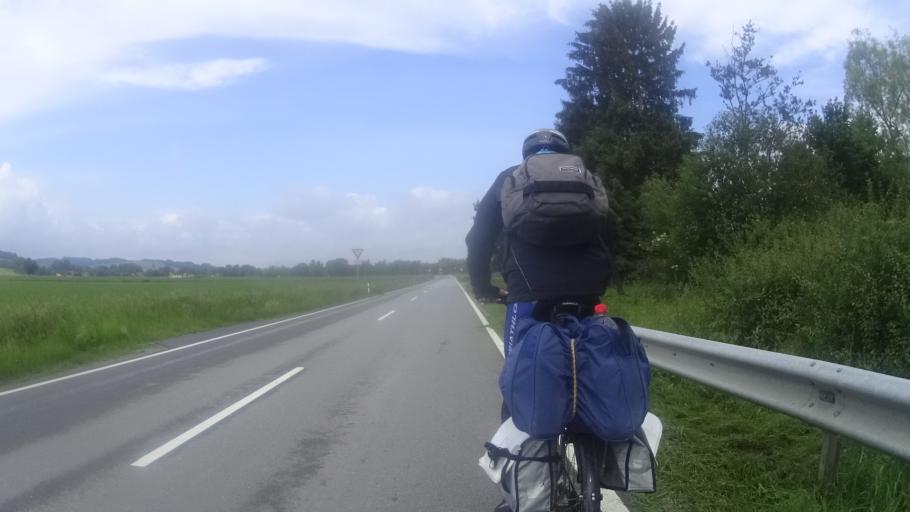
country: DE
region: Bavaria
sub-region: Lower Bavaria
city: Bad Birnbach
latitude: 48.4280
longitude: 13.1160
